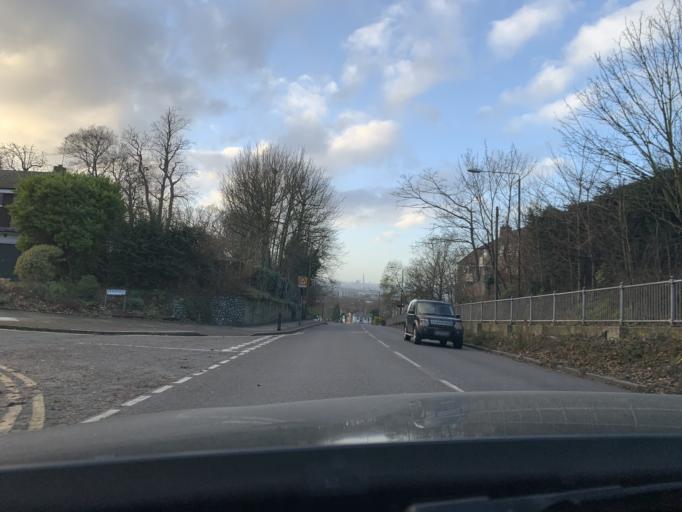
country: GB
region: England
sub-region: Greater London
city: Woolwich
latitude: 51.4697
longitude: 0.0630
